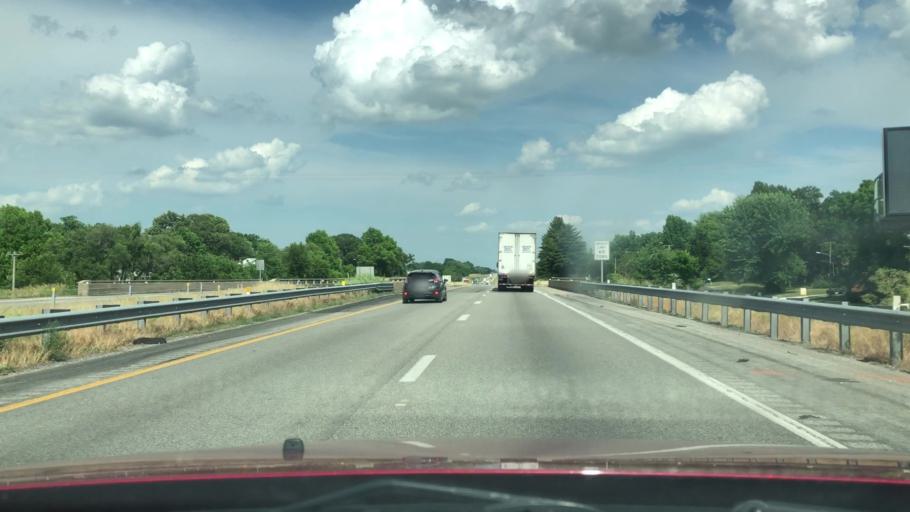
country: US
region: Missouri
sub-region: Greene County
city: Springfield
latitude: 37.2502
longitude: -93.2980
